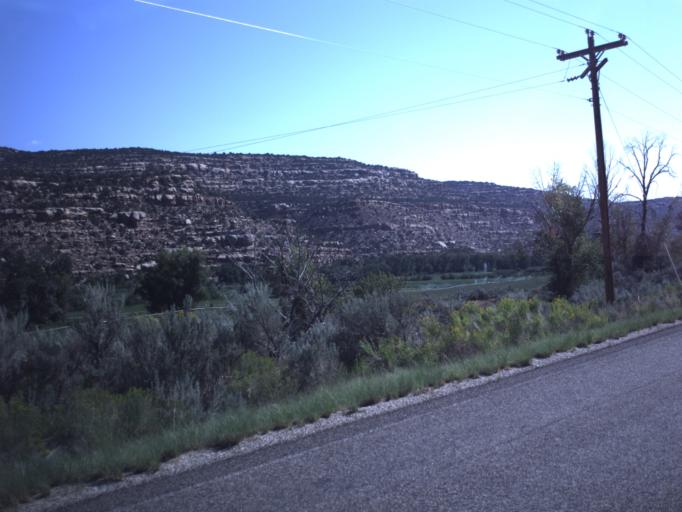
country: US
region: Utah
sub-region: Duchesne County
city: Duchesne
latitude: 40.2960
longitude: -110.5532
